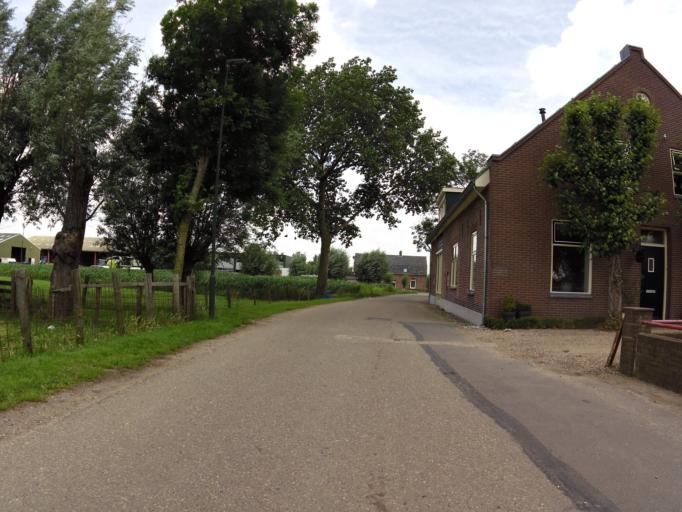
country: NL
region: South Holland
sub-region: Gemeente Gorinchem
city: Gorinchem
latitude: 51.8924
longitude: 4.9711
